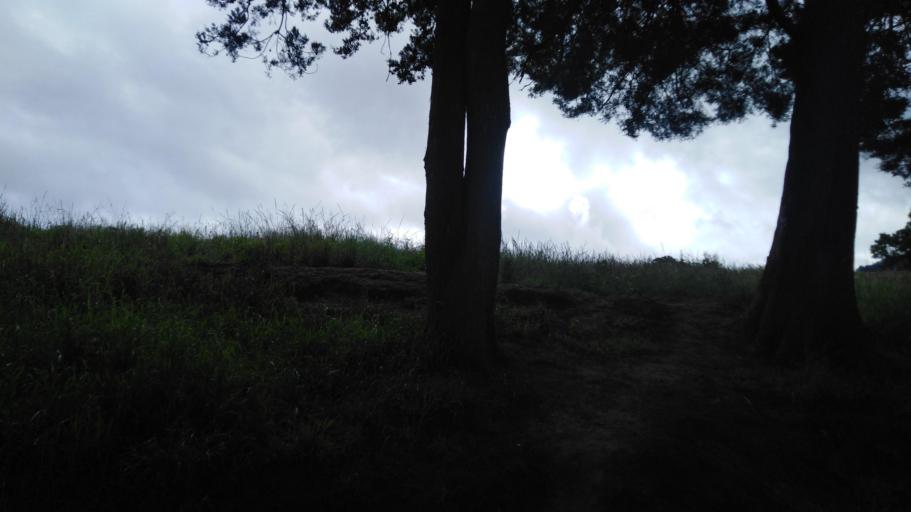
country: GT
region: Quetzaltenango
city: Quetzaltenango
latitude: 14.8517
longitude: -91.5054
